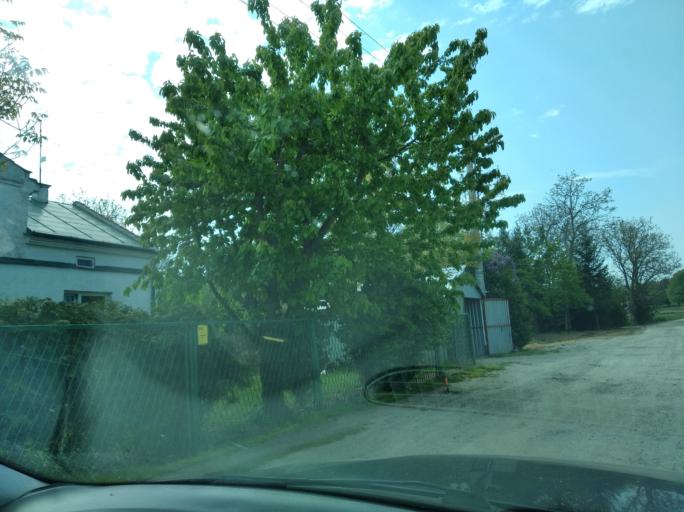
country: PL
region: Subcarpathian Voivodeship
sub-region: Powiat jaroslawski
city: Jaroslaw
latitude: 50.0006
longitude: 22.6801
